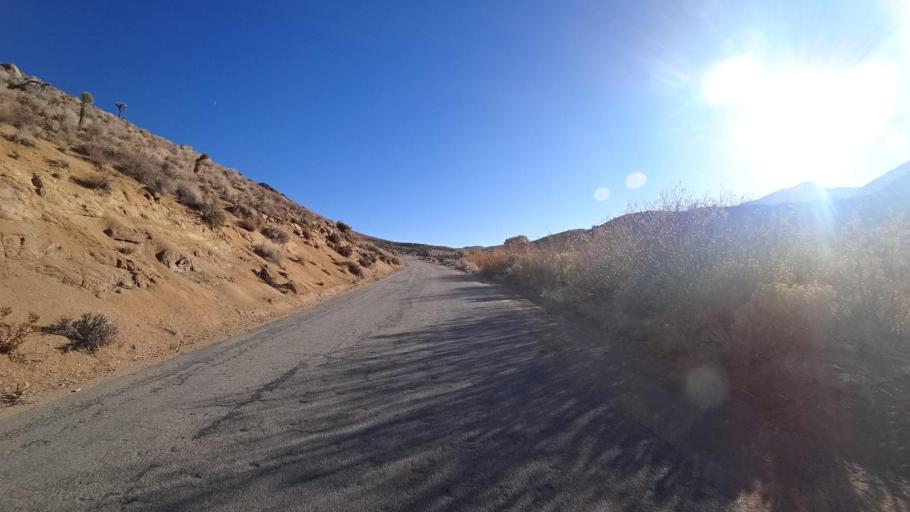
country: US
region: California
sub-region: Kern County
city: Weldon
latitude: 35.4764
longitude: -118.2117
